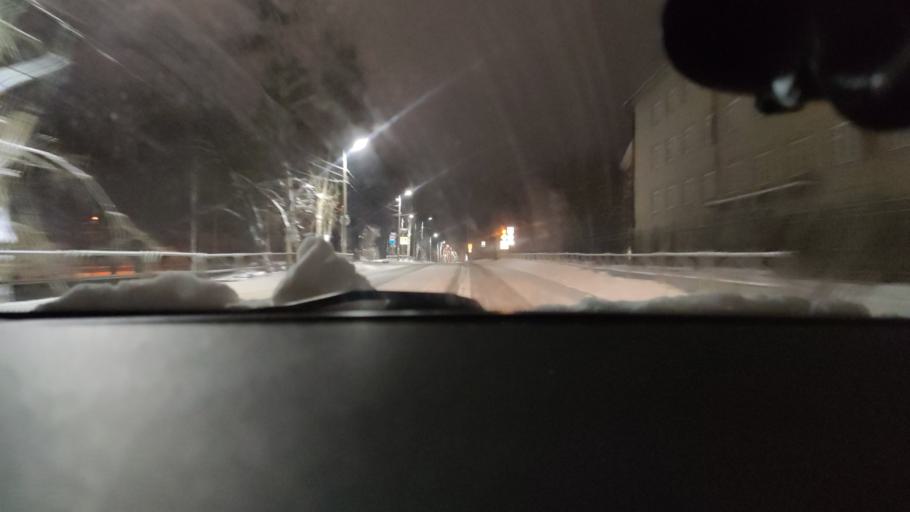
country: RU
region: Perm
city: Krasnokamsk
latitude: 58.0846
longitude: 55.7458
